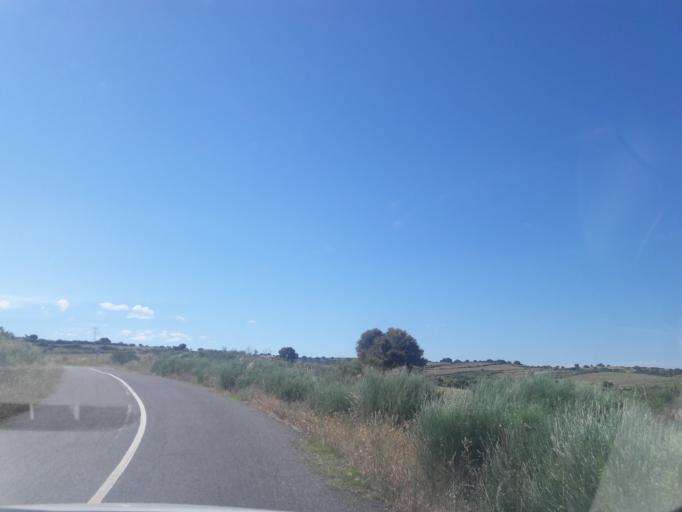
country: ES
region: Castille and Leon
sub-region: Provincia de Salamanca
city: Saucelle
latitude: 40.9934
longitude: -6.7335
